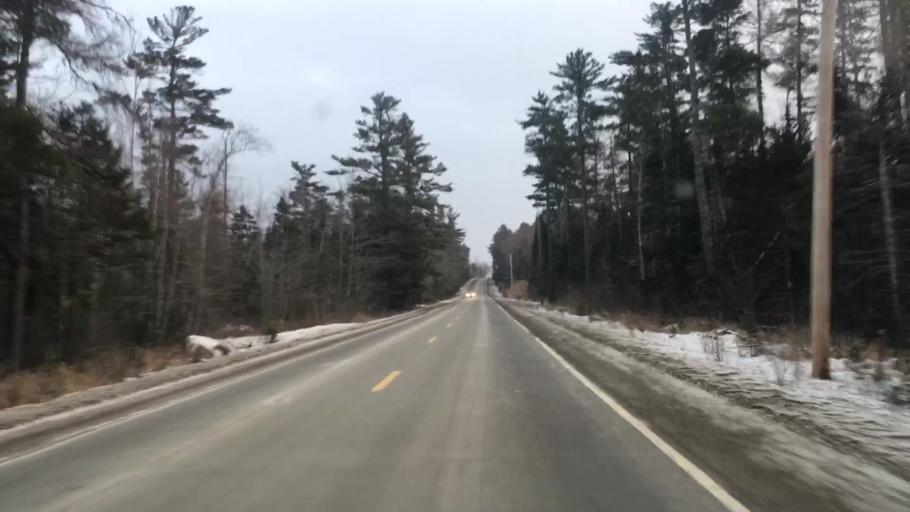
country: US
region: Maine
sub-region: Hancock County
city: Ellsworth
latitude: 44.6780
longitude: -68.3527
